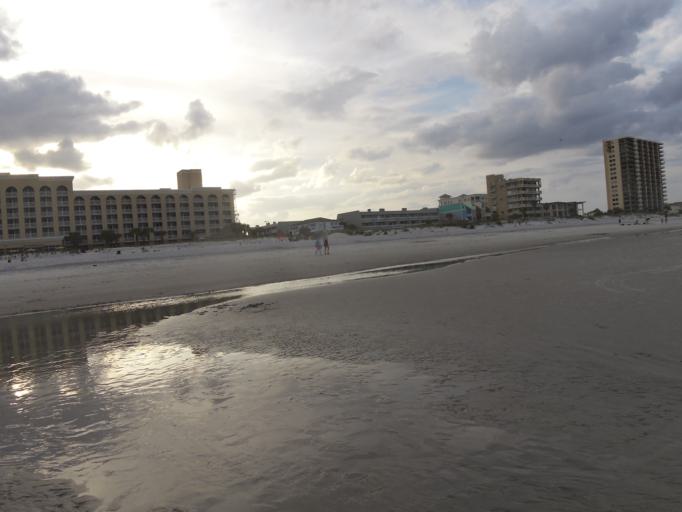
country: US
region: Florida
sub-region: Duval County
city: Jacksonville Beach
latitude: 30.3040
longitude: -81.3904
